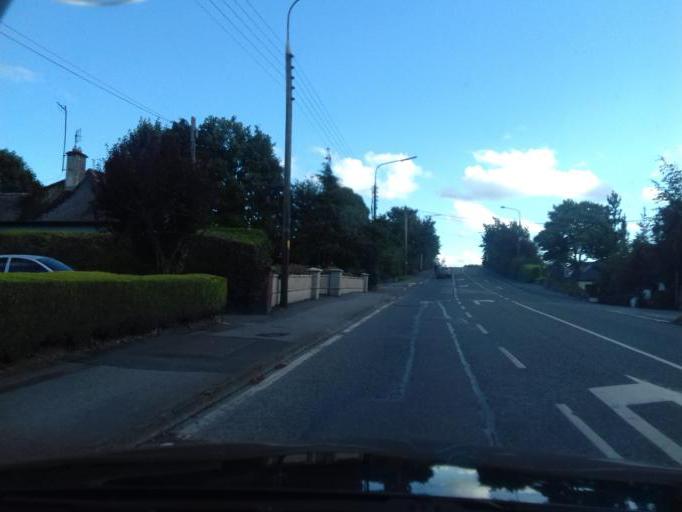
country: IE
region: Leinster
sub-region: Uibh Fhaili
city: Tullamore
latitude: 53.2664
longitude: -7.4864
